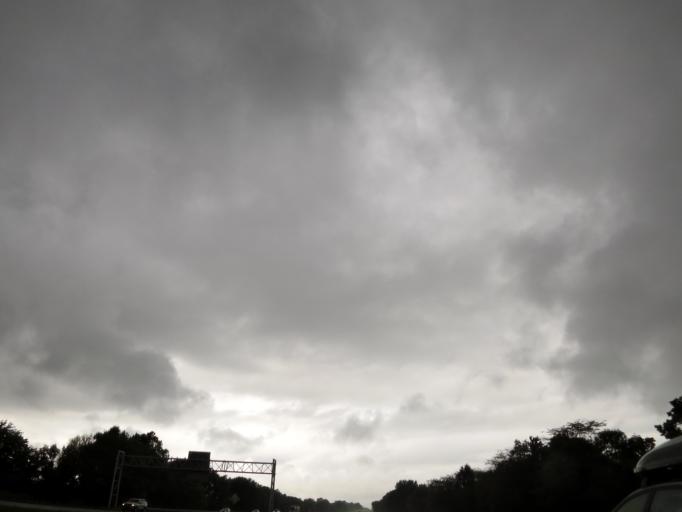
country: US
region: Illinois
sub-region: Jefferson County
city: Mount Vernon
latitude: 38.3450
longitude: -88.9746
